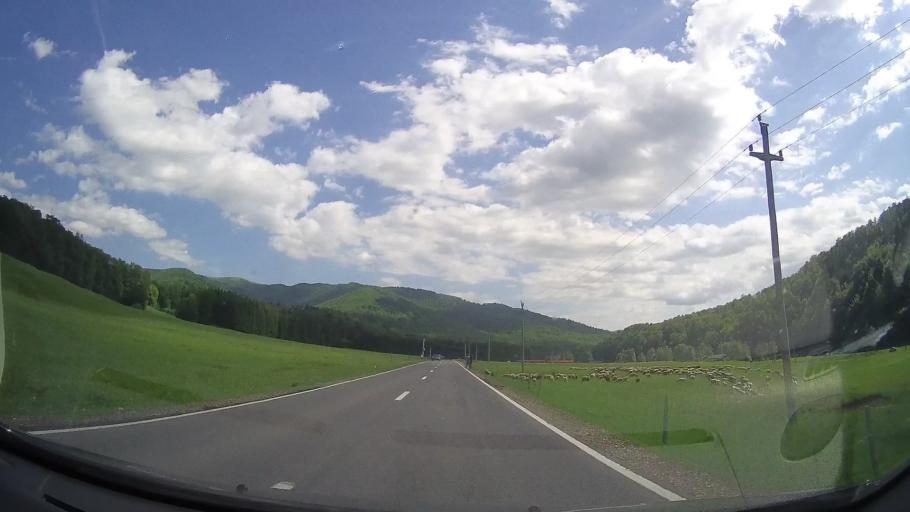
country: RO
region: Prahova
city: Maneciu
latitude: 45.4230
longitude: 25.9419
